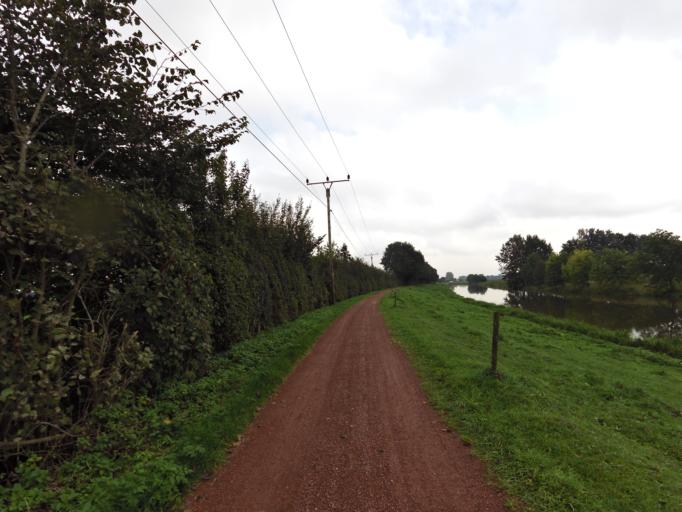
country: DE
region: North Rhine-Westphalia
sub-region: Regierungsbezirk Dusseldorf
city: Bocholt
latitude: 51.8494
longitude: 6.5420
